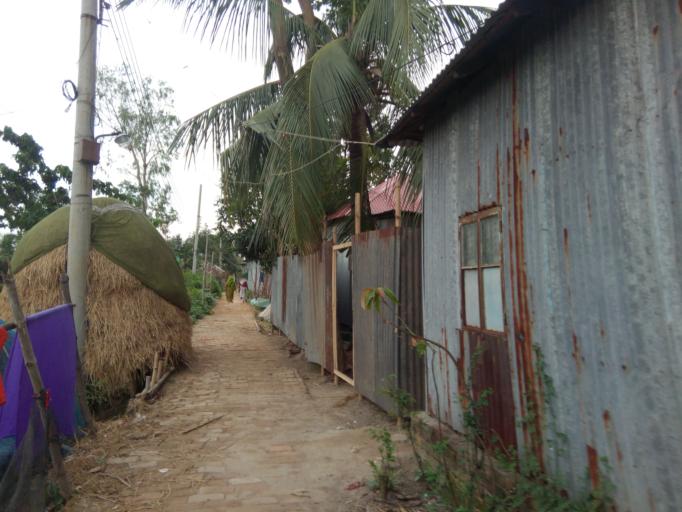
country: BD
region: Dhaka
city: Paltan
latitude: 23.7390
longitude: 90.4659
